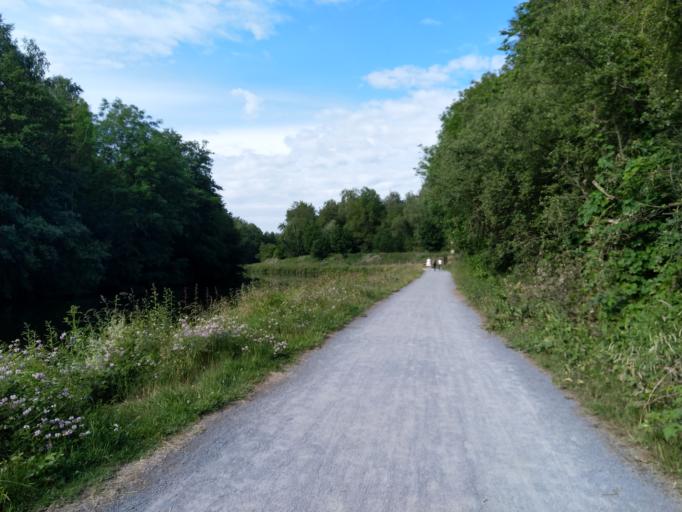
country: FR
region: Nord-Pas-de-Calais
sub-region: Departement du Nord
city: Marpent
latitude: 50.2911
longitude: 4.0712
